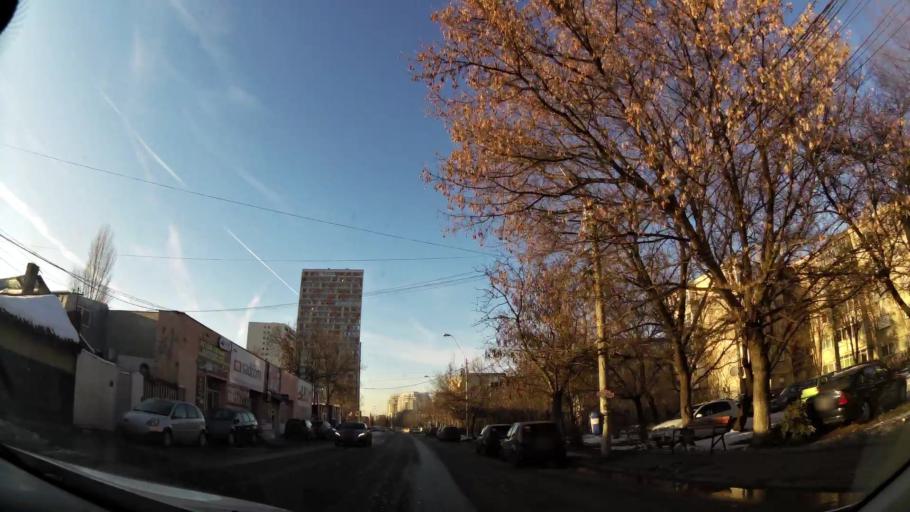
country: RO
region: Ilfov
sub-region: Comuna Fundeni-Dobroesti
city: Fundeni
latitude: 44.4501
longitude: 26.1479
